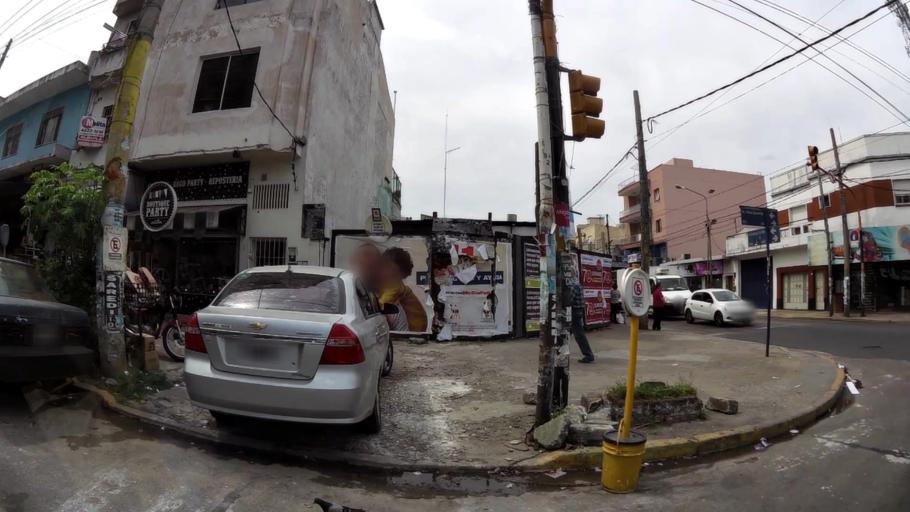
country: AR
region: Buenos Aires F.D.
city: Villa Lugano
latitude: -34.6979
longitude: -58.5066
